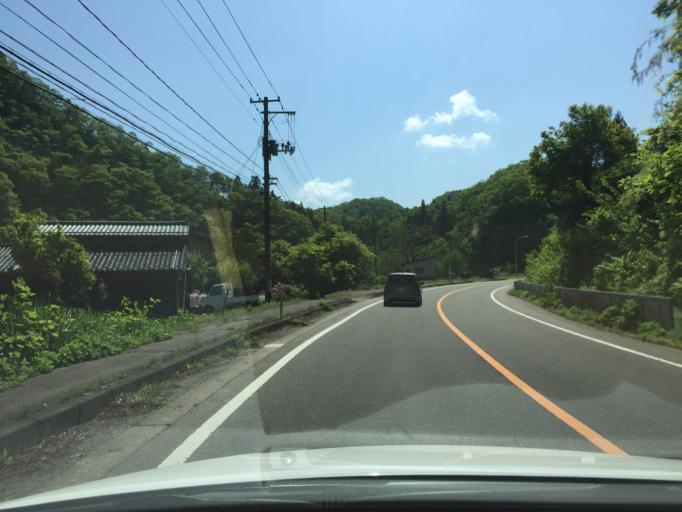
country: JP
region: Niigata
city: Kamo
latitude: 37.6264
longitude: 139.1022
